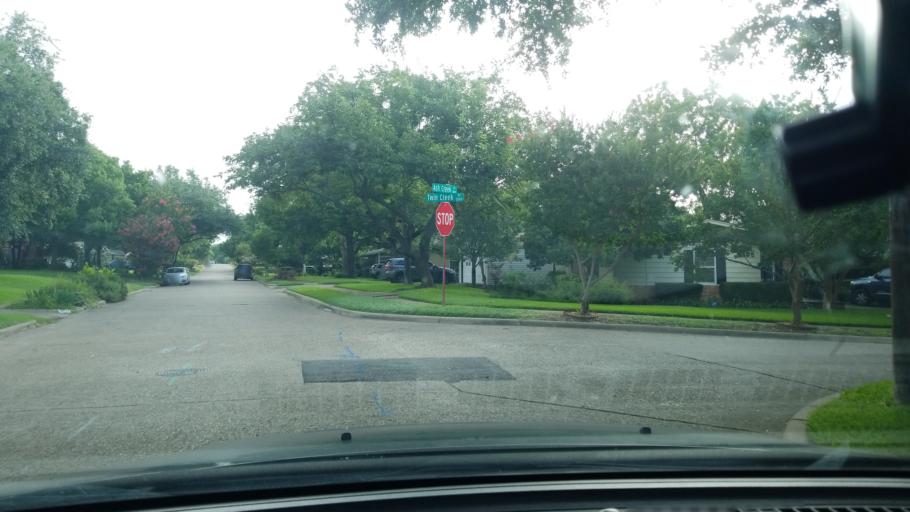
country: US
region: Texas
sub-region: Dallas County
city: Garland
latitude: 32.8249
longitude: -96.6902
